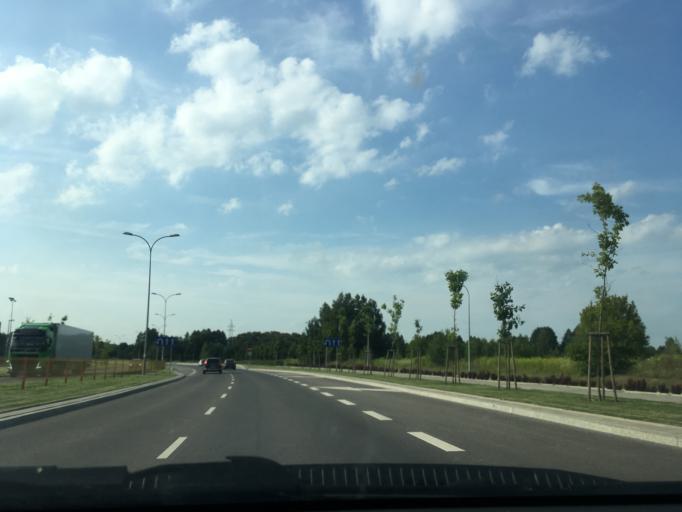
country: PL
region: Podlasie
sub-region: Bialystok
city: Bialystok
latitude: 53.1354
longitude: 23.2211
